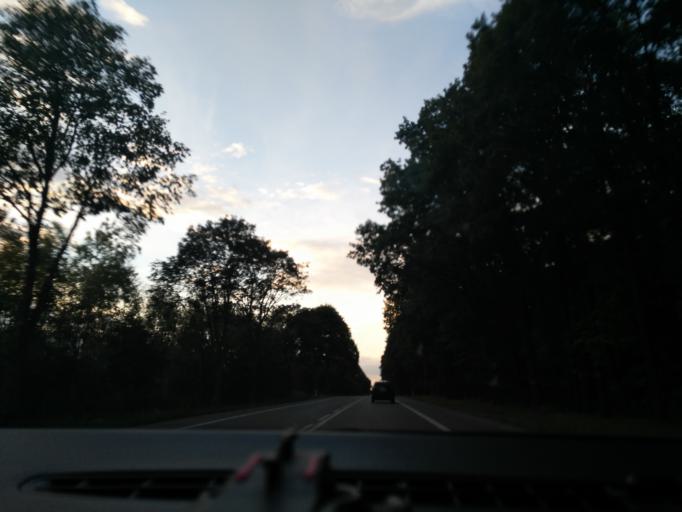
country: PL
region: Lublin Voivodeship
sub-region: Powiat lubelski
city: Niemce
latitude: 51.3934
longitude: 22.6363
